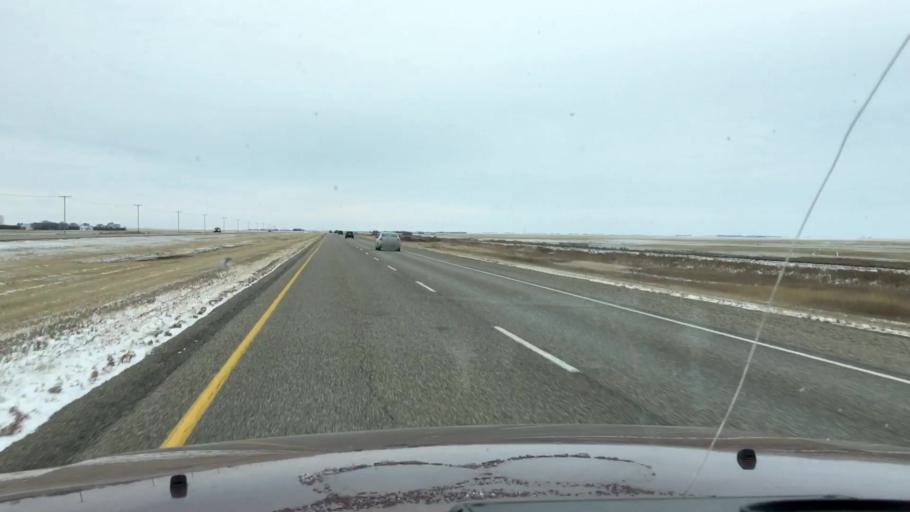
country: CA
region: Saskatchewan
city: Watrous
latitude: 51.1388
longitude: -105.9015
